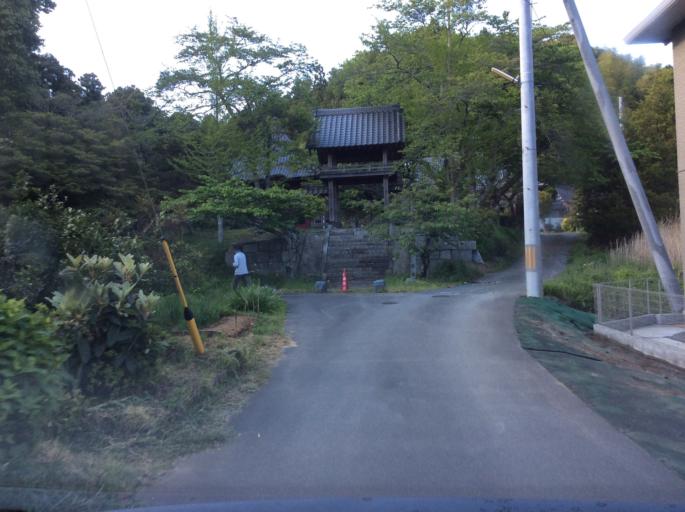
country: JP
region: Fukushima
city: Iwaki
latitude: 36.9876
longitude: 140.8425
